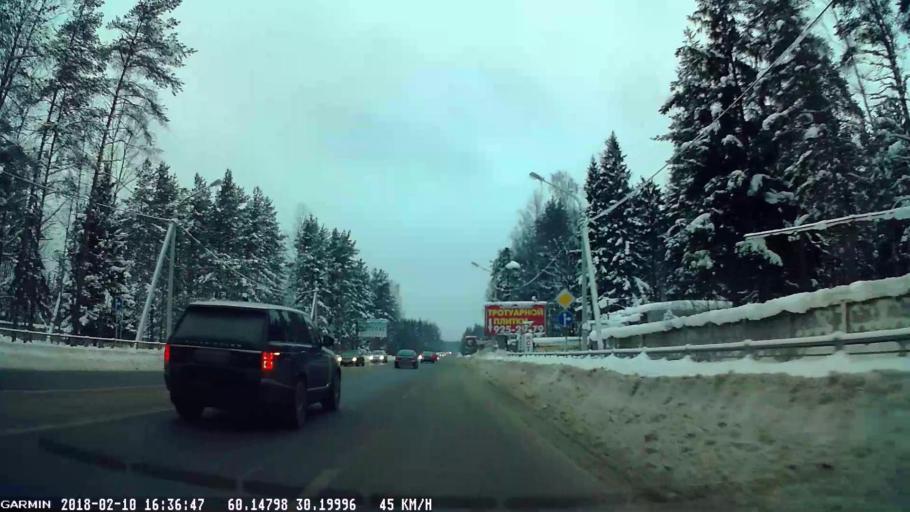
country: RU
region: Leningrad
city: Sertolovo
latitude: 60.1479
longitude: 30.2000
